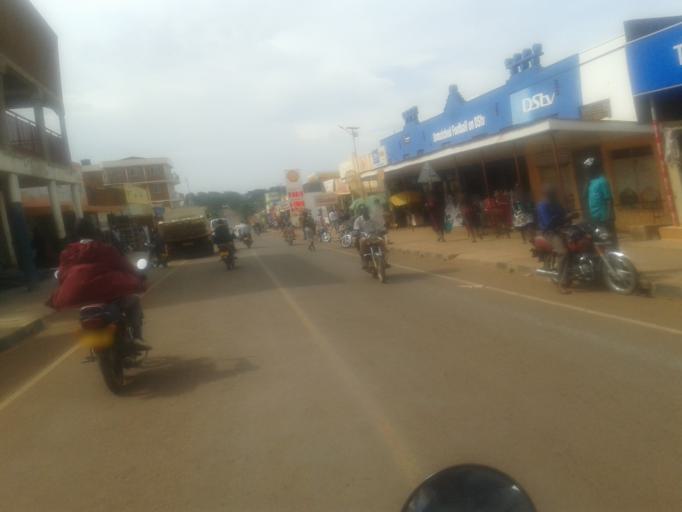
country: UG
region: Northern Region
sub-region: Gulu District
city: Gulu
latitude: 2.7692
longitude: 32.2982
